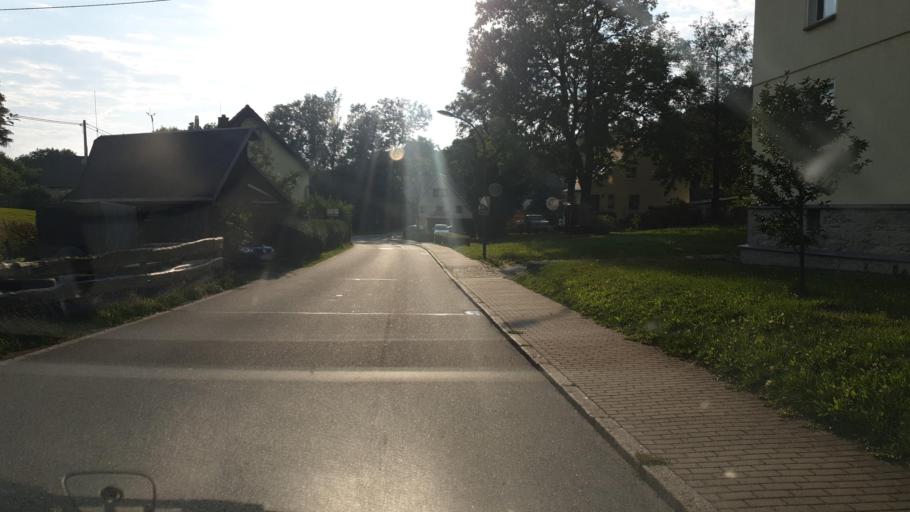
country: DE
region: Saxony
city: Zwonitz
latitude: 50.6330
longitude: 12.7754
